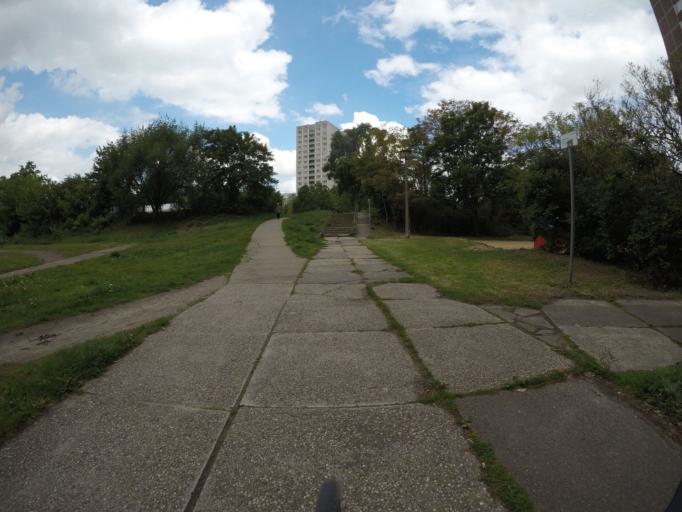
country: DE
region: Berlin
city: Marzahn
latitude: 52.5515
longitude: 13.5573
